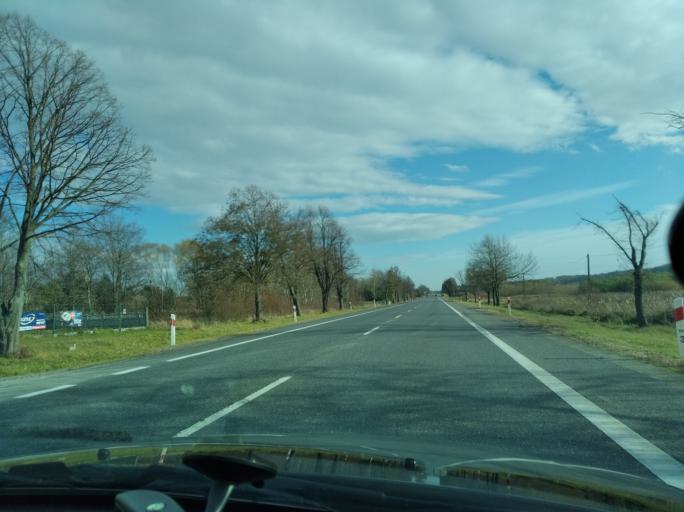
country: PL
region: Subcarpathian Voivodeship
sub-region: Powiat debicki
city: Brzeznica
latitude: 50.0605
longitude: 21.4892
